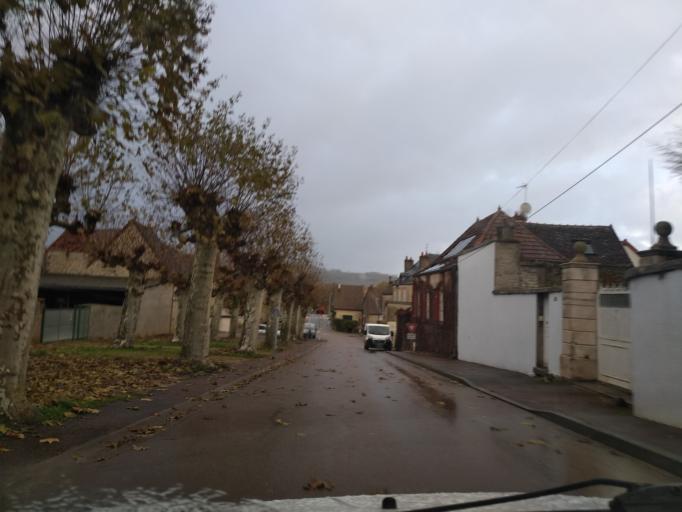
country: FR
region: Bourgogne
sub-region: Departement de Saone-et-Loire
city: Saint-Leger-sur-Dheune
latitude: 46.8782
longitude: 4.6639
